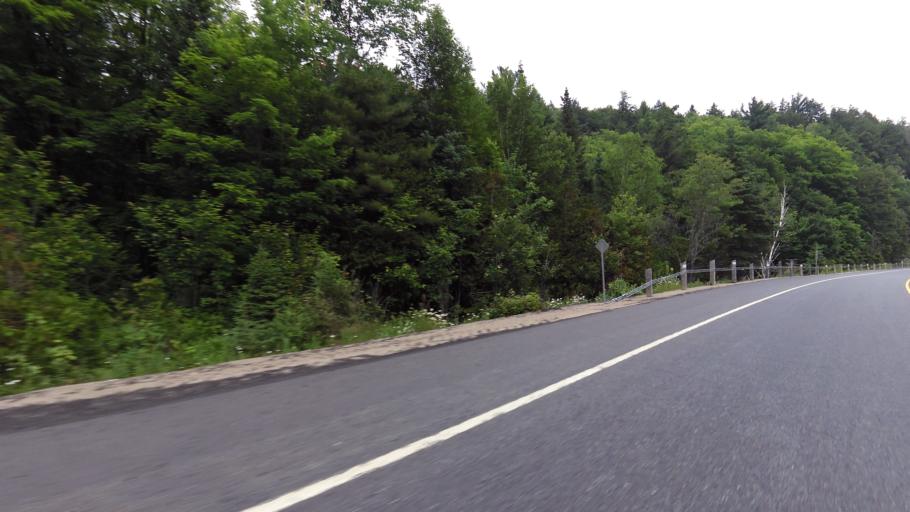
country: CA
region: Ontario
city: Huntsville
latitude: 45.5237
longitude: -78.7106
